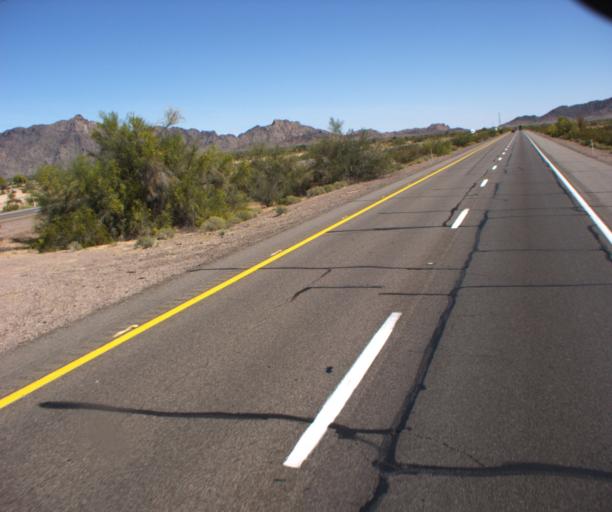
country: US
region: Arizona
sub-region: Yuma County
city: Wellton
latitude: 32.7172
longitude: -113.7961
